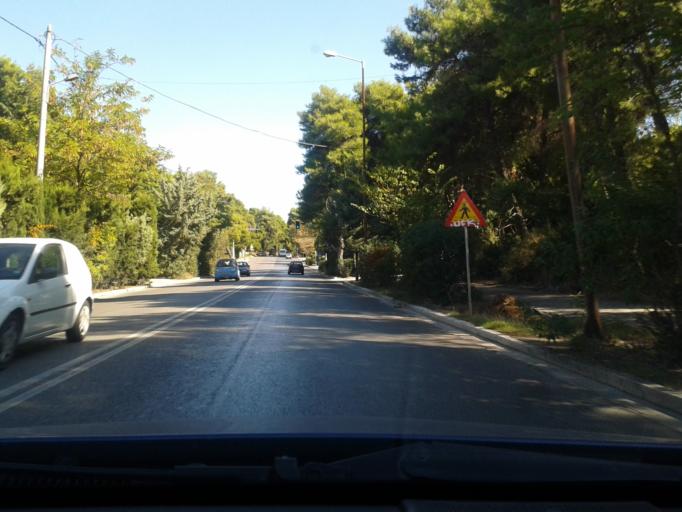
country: GR
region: Attica
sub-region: Nomarchia Athinas
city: Ekali
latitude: 38.1095
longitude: 23.8407
